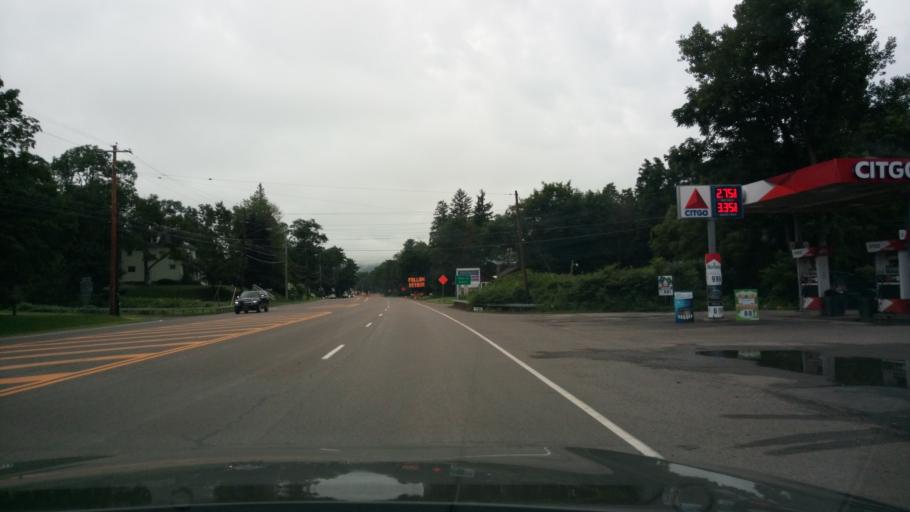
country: US
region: New York
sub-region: Chemung County
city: West Elmira
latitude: 42.0836
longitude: -76.8619
